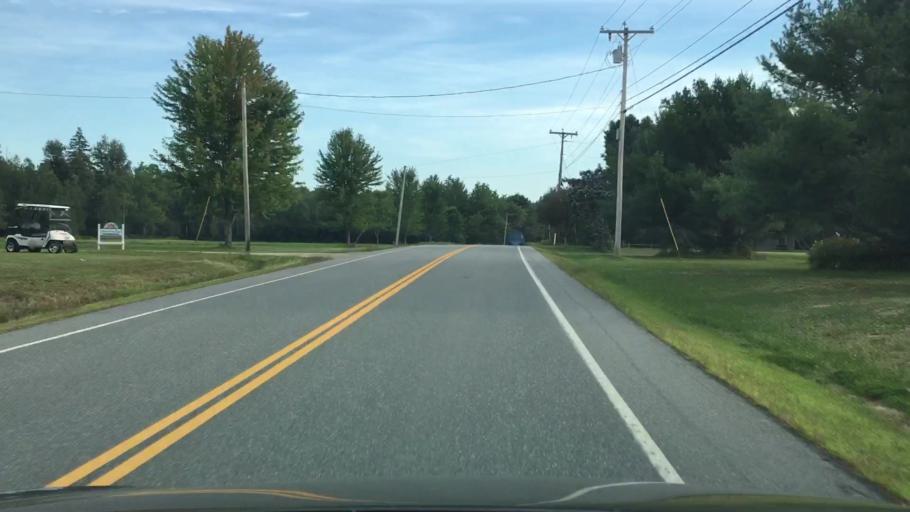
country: US
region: Maine
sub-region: Hancock County
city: Penobscot
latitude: 44.4585
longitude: -68.7804
